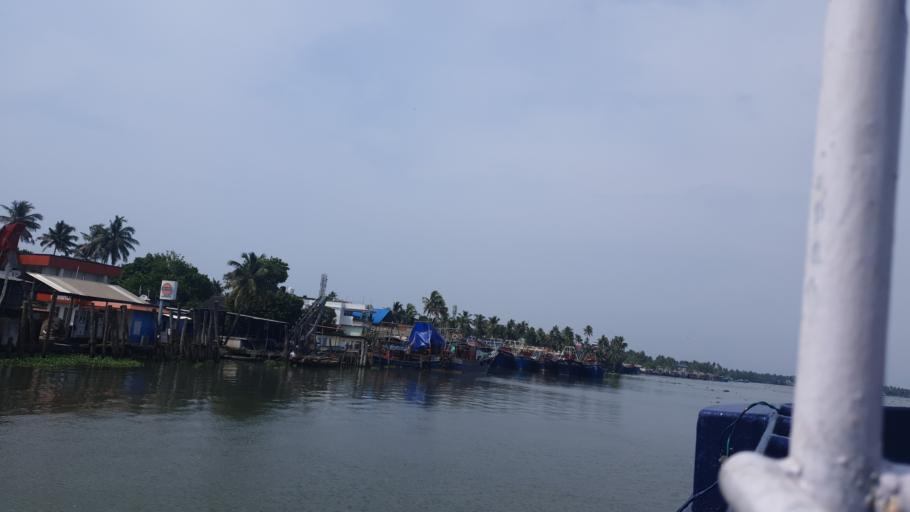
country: IN
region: Kerala
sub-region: Ernakulam
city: Cochin
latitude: 9.9867
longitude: 76.2412
